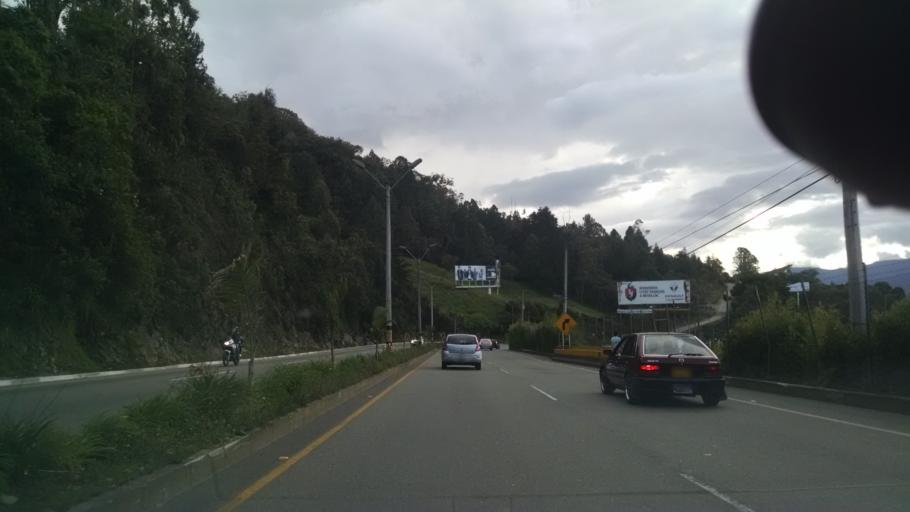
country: CO
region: Antioquia
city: Envigado
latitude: 6.1526
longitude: -75.5438
